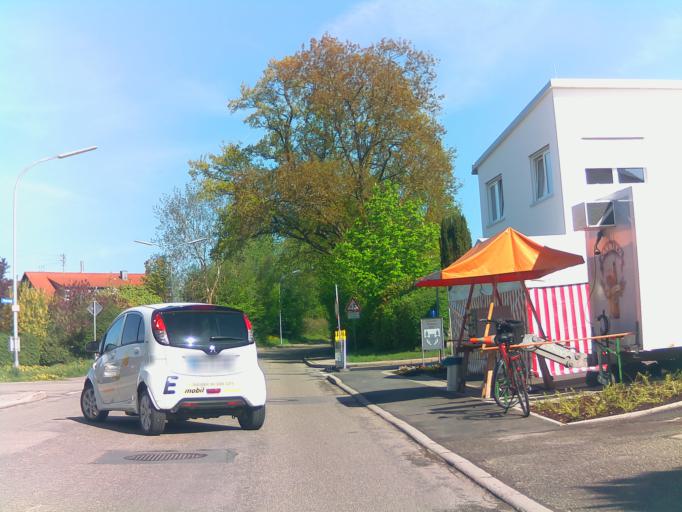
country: DE
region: Baden-Wuerttemberg
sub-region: Karlsruhe Region
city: Altensteig
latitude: 48.6204
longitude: 8.6445
